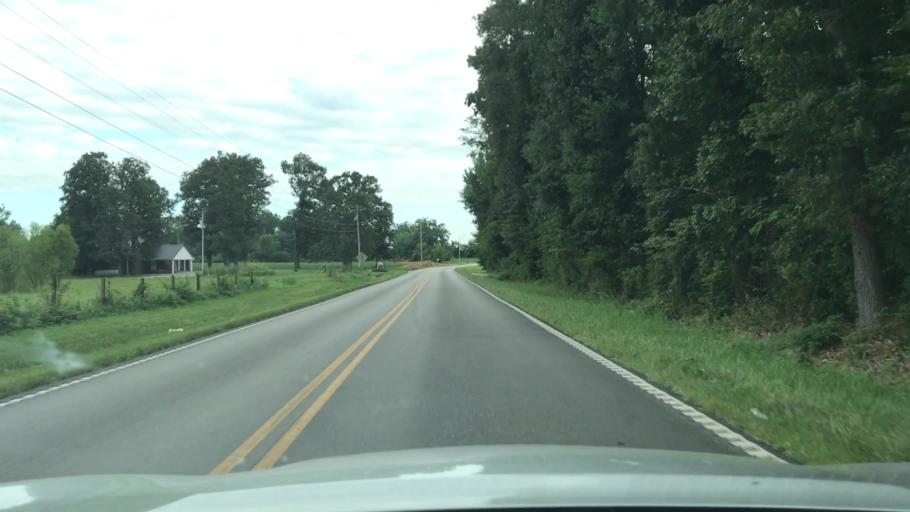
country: US
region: Kentucky
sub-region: Todd County
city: Guthrie
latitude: 36.7278
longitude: -87.1894
